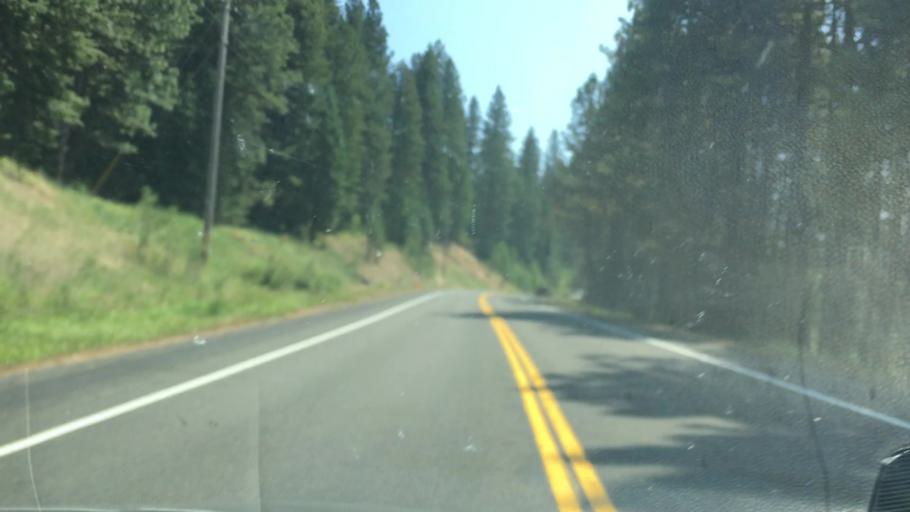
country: US
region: Idaho
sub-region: Valley County
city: McCall
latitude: 45.1131
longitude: -116.3024
